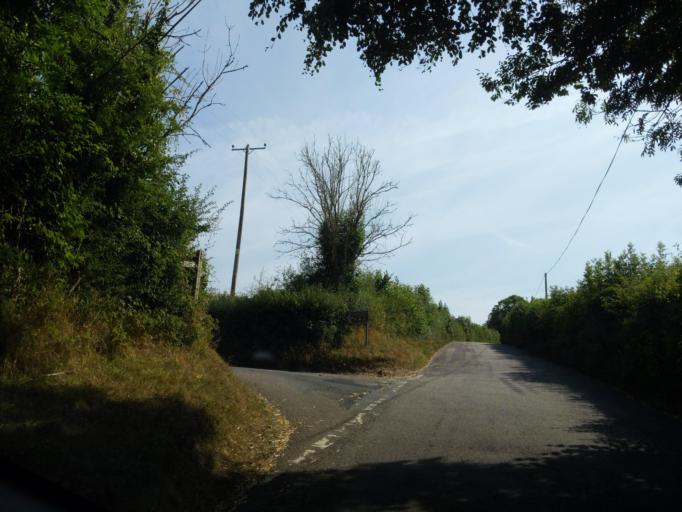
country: GB
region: England
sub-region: Devon
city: Winkleigh
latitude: 50.8851
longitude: -3.8732
